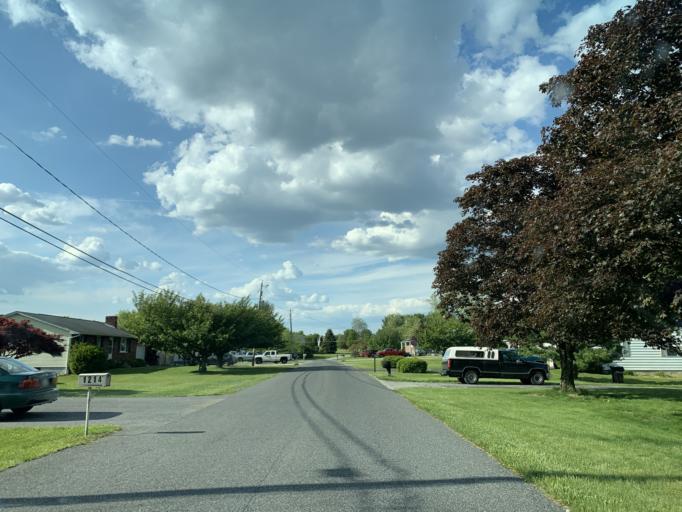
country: US
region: Maryland
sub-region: Carroll County
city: Westminster
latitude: 39.6076
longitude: -76.9414
